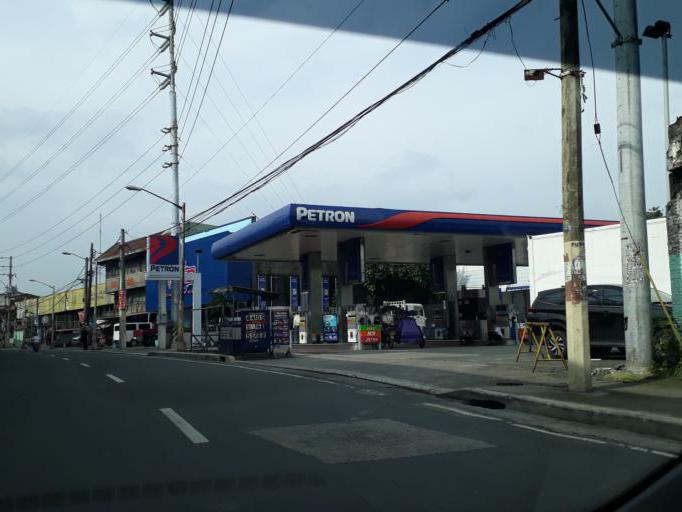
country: PH
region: Metro Manila
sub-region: City of Manila
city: Manila
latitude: 14.6377
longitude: 120.9832
